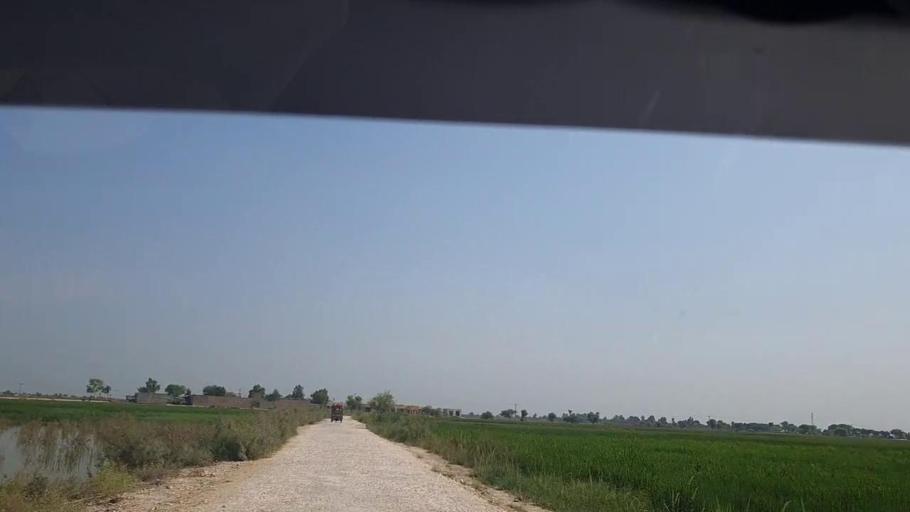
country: PK
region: Sindh
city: Thul
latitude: 28.1960
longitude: 68.7330
